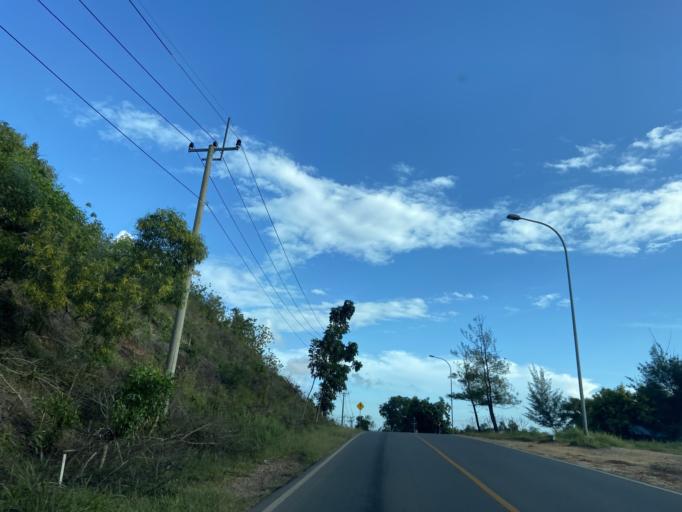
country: SG
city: Singapore
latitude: 0.9956
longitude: 104.0328
